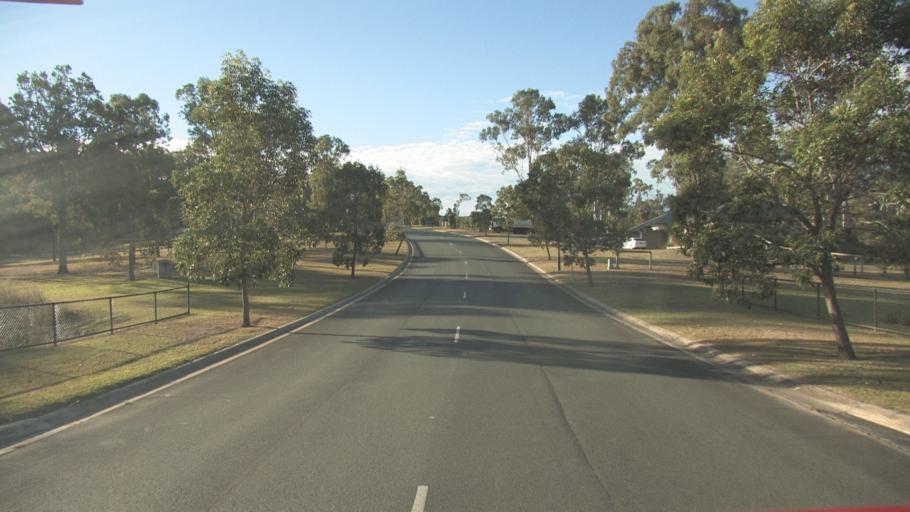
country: AU
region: Queensland
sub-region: Logan
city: Cedar Vale
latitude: -27.8719
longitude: 153.0763
